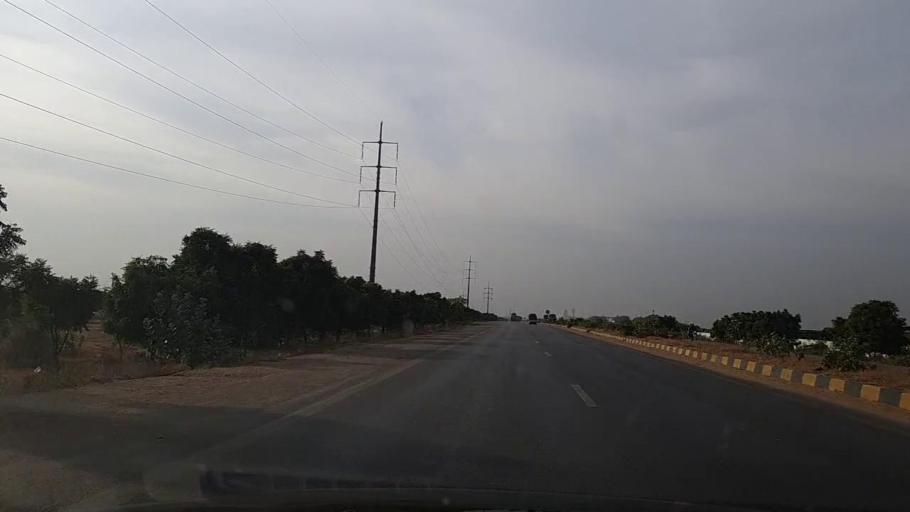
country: PK
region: Sindh
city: Gharo
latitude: 24.8337
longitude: 67.4585
